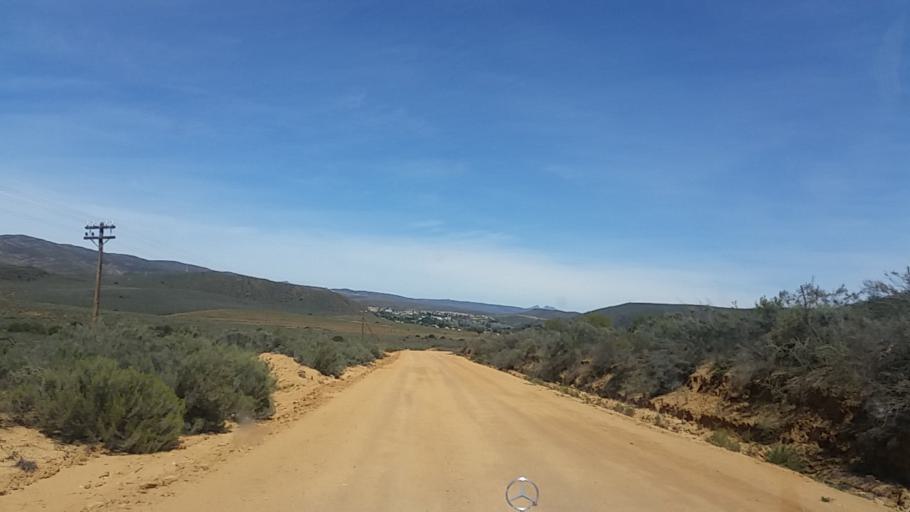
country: ZA
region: Western Cape
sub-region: Eden District Municipality
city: Knysna
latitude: -33.6376
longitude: 23.1515
